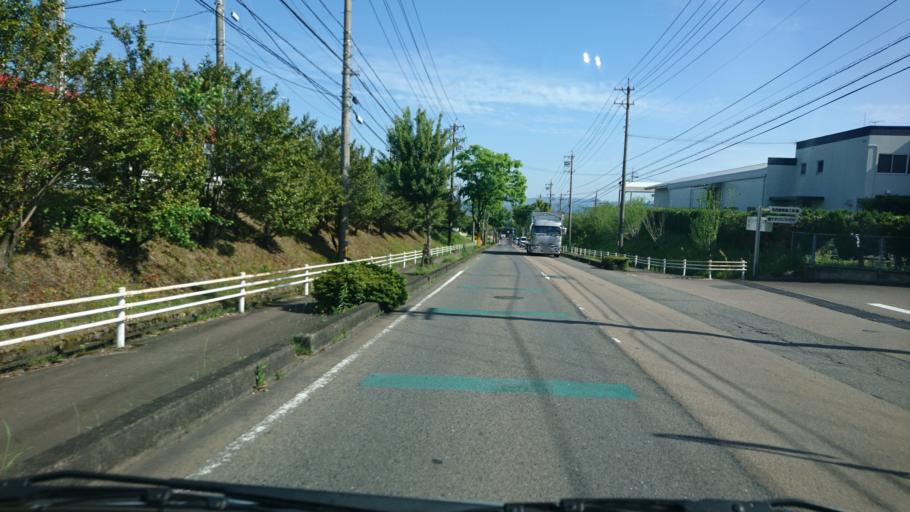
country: JP
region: Gifu
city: Minokamo
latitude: 35.4047
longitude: 137.0474
